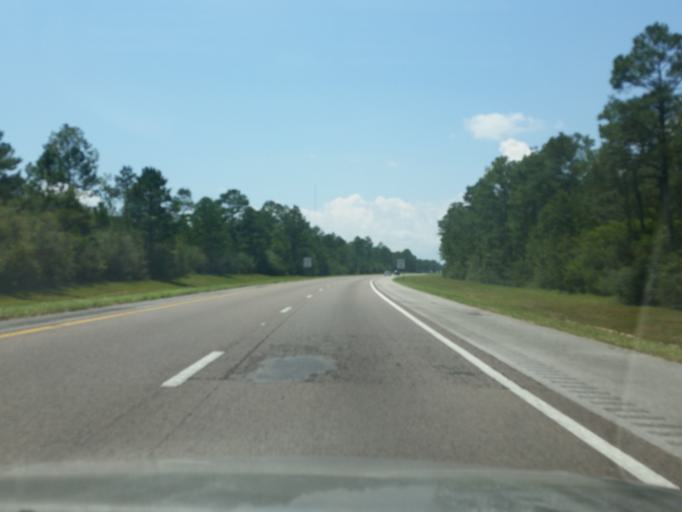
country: US
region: Florida
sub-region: Escambia County
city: Cantonment
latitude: 30.5816
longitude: -87.5163
